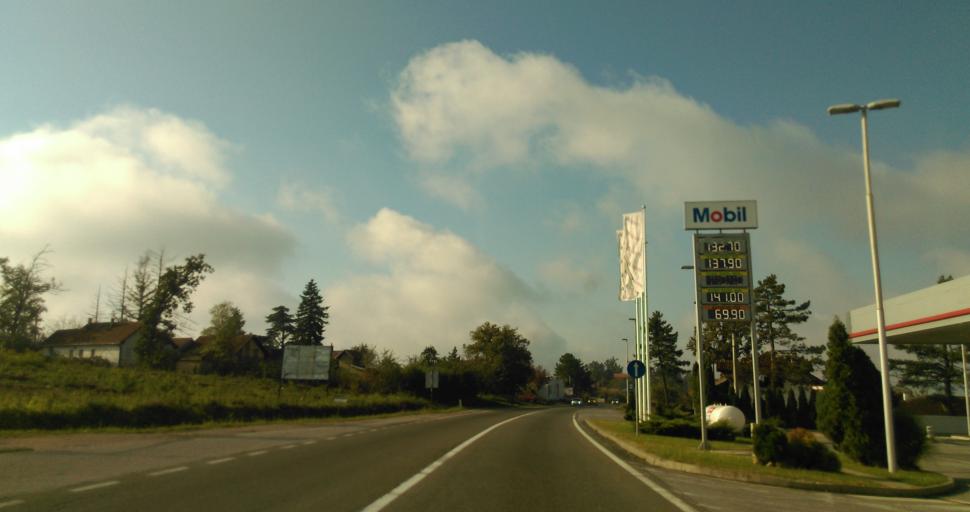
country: RS
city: Vranic
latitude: 44.5946
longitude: 20.3502
